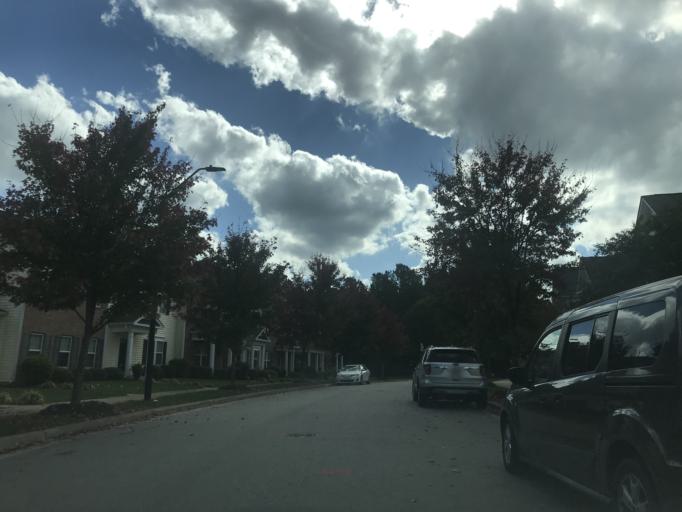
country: US
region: North Carolina
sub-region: Wake County
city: Raleigh
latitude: 35.7381
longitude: -78.6541
